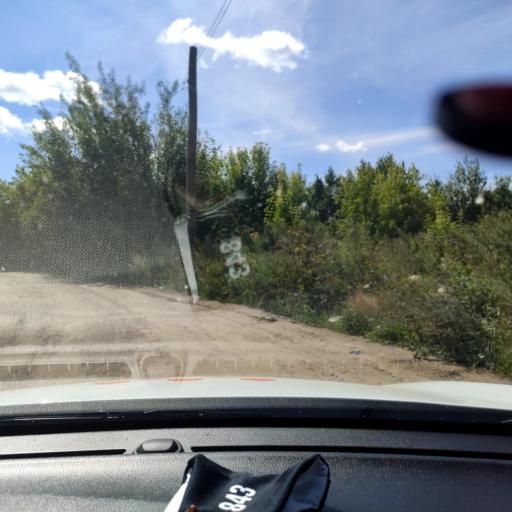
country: RU
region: Tatarstan
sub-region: Gorod Kazan'
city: Kazan
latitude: 55.8229
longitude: 49.2004
